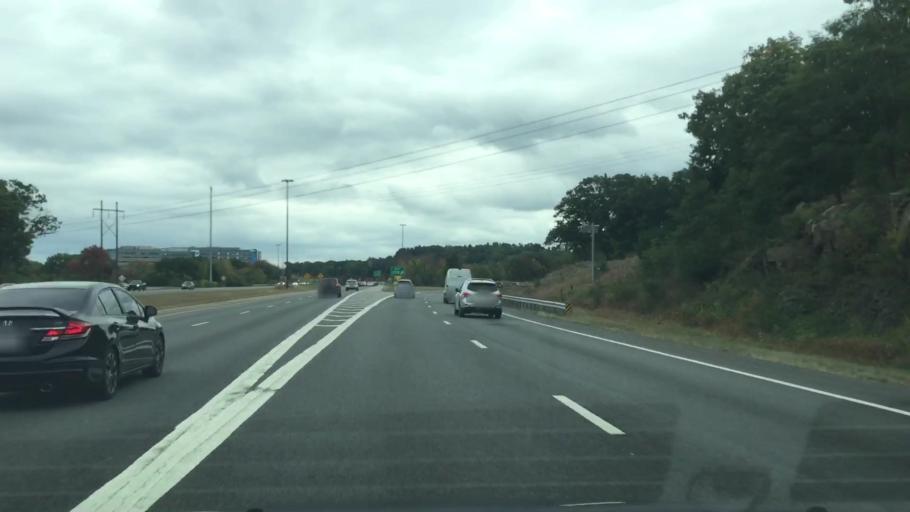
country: US
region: Massachusetts
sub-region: Middlesex County
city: Lexington
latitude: 42.4809
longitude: -71.2231
